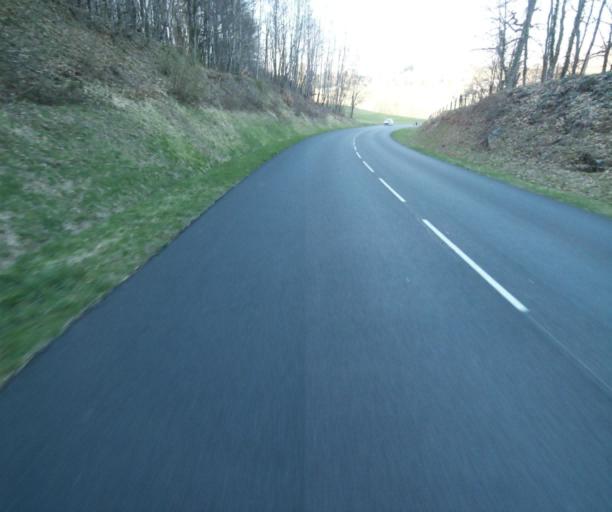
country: FR
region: Limousin
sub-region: Departement de la Correze
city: Seilhac
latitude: 45.3563
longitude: 1.7086
